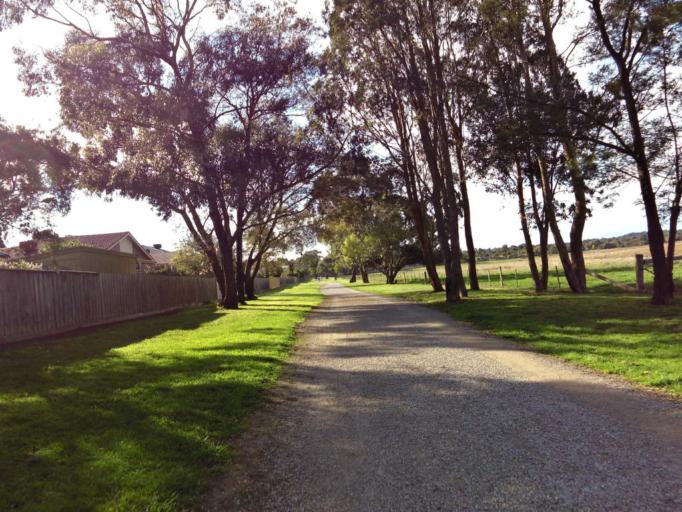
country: AU
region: Victoria
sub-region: Whitehorse
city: Vermont South
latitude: -37.8720
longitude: 145.1883
